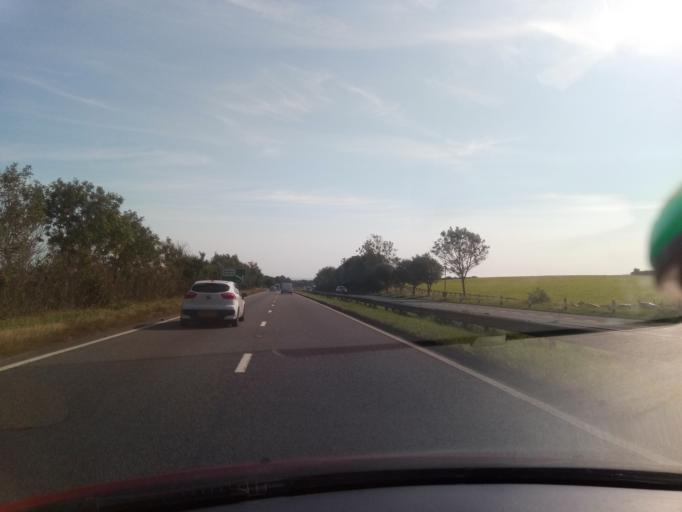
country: GB
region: England
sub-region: Sunderland
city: Ryhope
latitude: 54.8488
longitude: -1.3865
